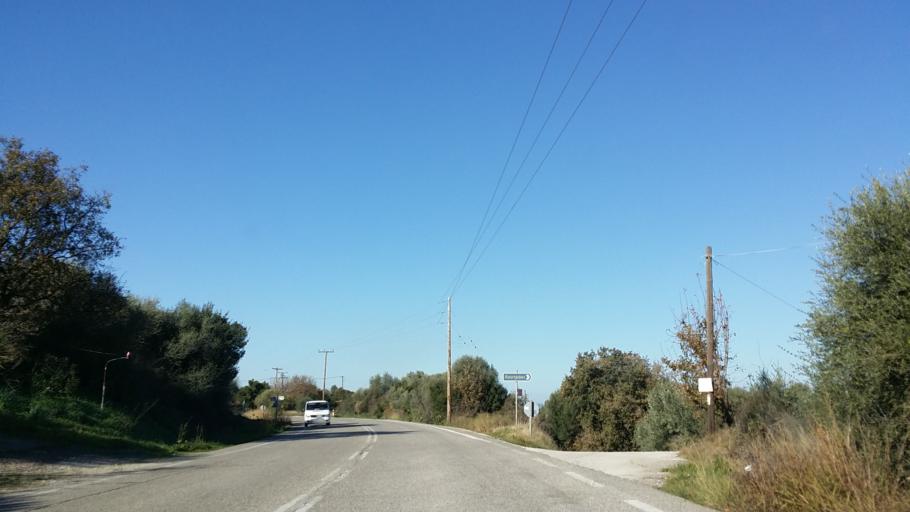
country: GR
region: West Greece
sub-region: Nomos Aitolias kai Akarnanias
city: Amfilochia
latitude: 38.8654
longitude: 21.0750
